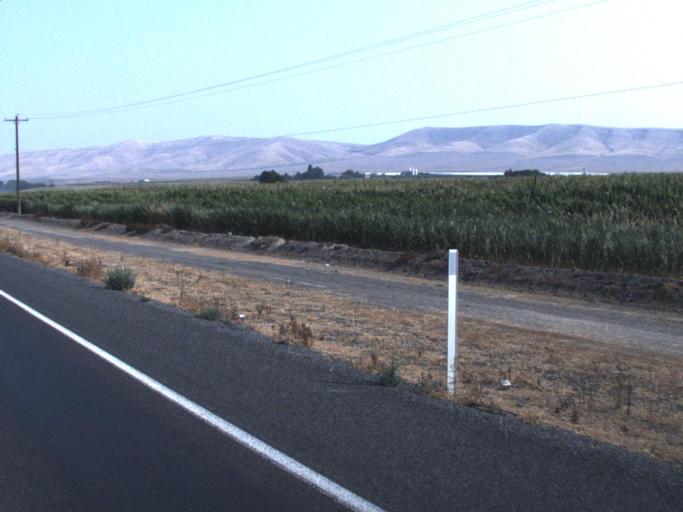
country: US
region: Washington
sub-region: Yakima County
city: Mabton
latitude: 46.1985
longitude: -119.9460
